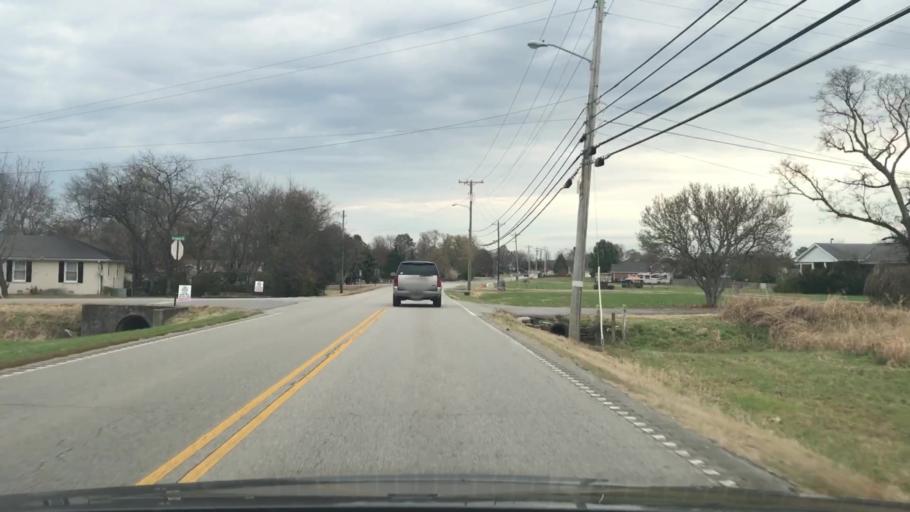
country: US
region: Tennessee
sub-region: Wilson County
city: Lebanon
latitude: 36.2213
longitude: -86.2792
